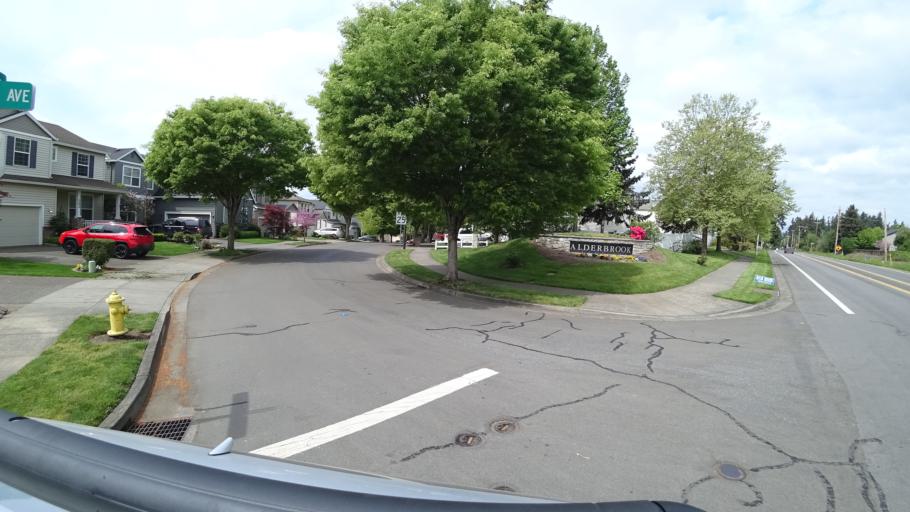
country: US
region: Oregon
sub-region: Washington County
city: Hillsboro
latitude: 45.5371
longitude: -122.9952
